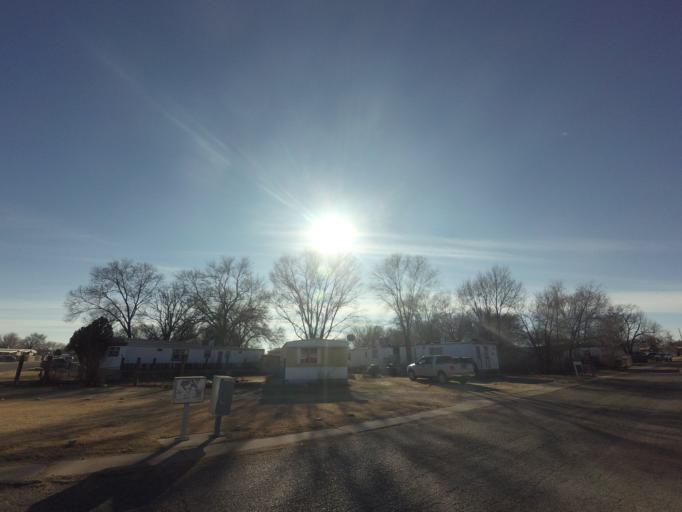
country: US
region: New Mexico
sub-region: Curry County
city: Clovis
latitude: 34.3885
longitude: -103.1986
